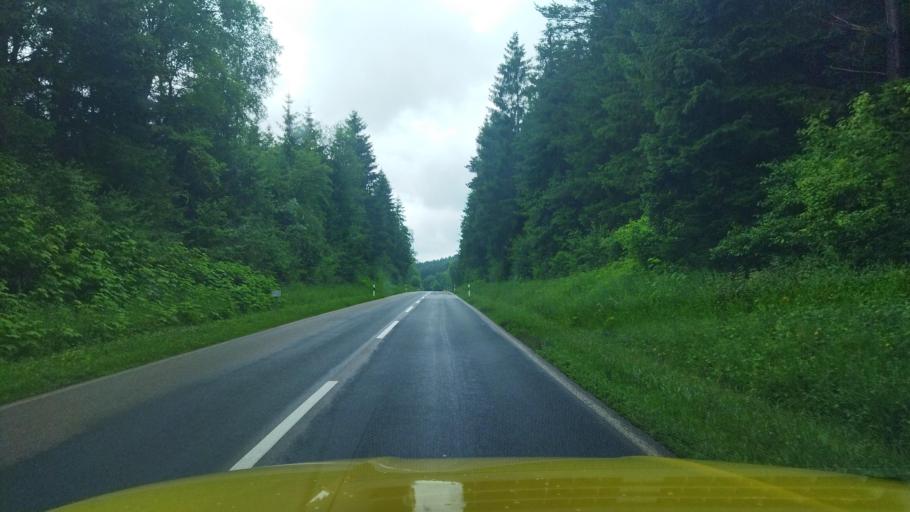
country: DE
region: Bavaria
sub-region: Lower Bavaria
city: Riedenburg
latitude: 48.9478
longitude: 11.6518
